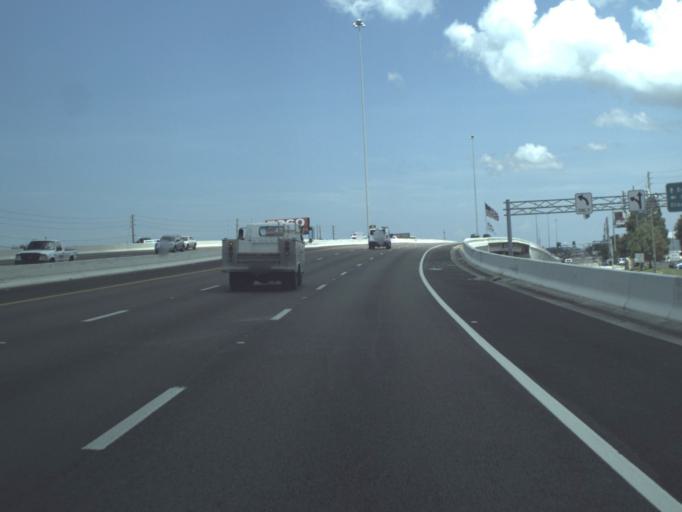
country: US
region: Florida
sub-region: Pinellas County
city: Dunedin
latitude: 28.0172
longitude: -82.7377
